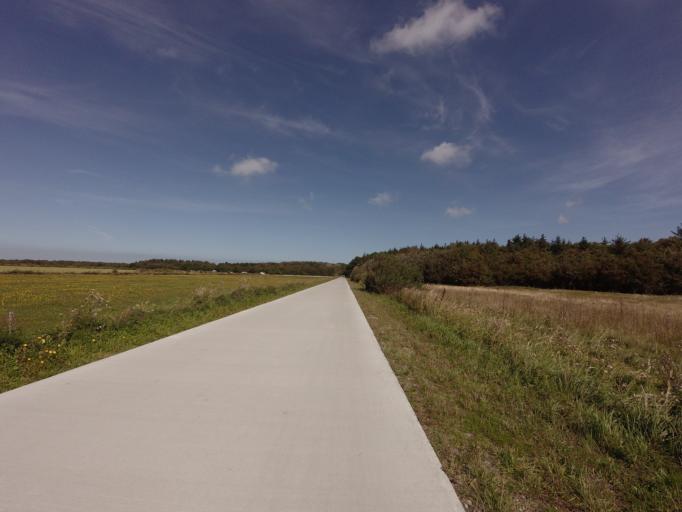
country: NL
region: Friesland
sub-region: Gemeente Ameland
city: Nes
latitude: 53.4491
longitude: 5.7573
